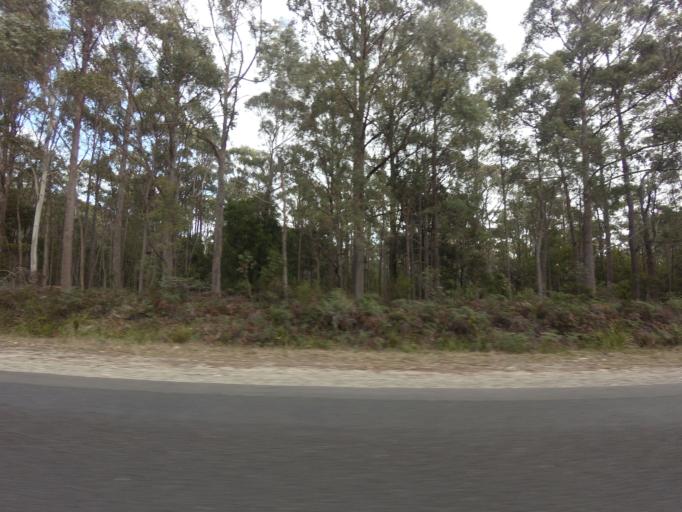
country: AU
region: Tasmania
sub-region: Meander Valley
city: Deloraine
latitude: -41.6149
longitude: 146.6904
